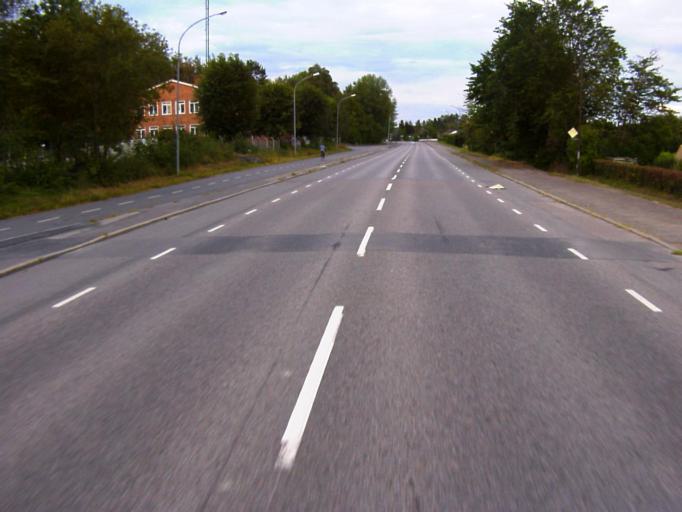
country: SE
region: Soedermanland
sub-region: Eskilstuna Kommun
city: Torshalla
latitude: 59.4016
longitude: 16.4858
